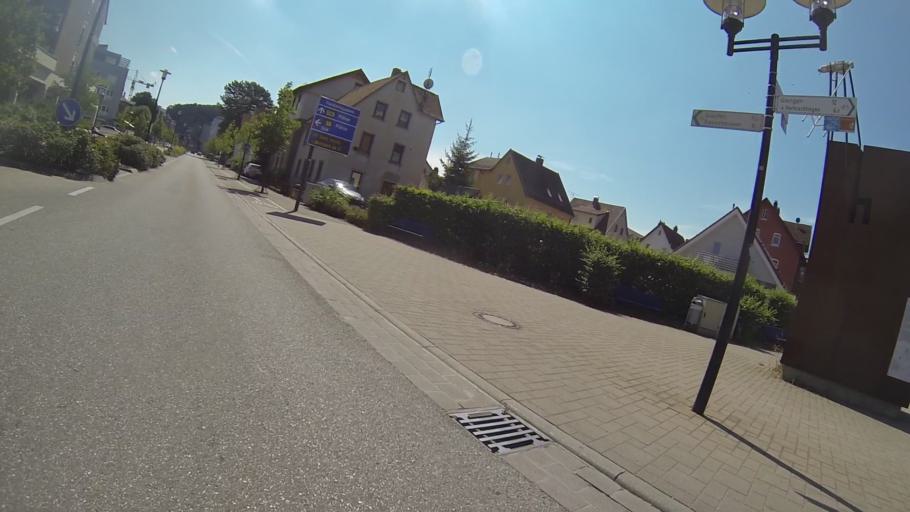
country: DE
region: Baden-Wuerttemberg
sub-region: Regierungsbezirk Stuttgart
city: Heidenheim an der Brenz
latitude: 48.6746
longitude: 10.1520
